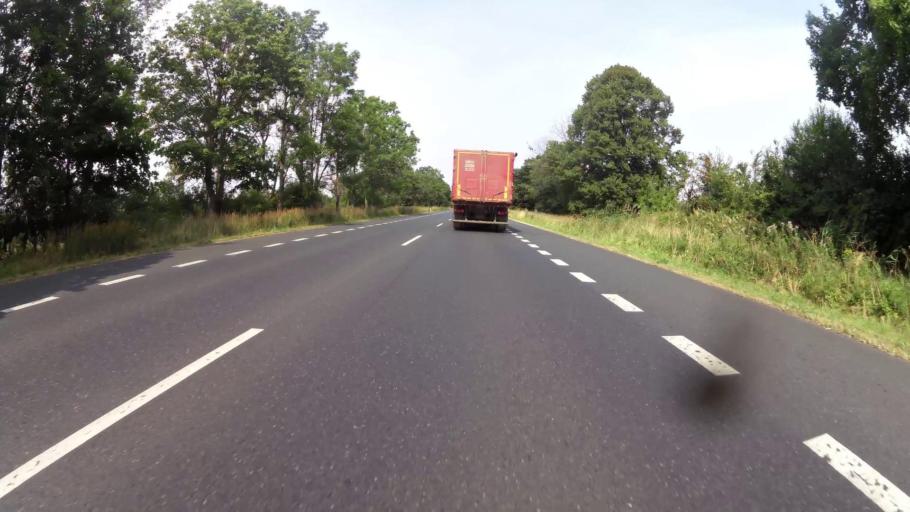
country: PL
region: West Pomeranian Voivodeship
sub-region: Powiat pyrzycki
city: Lipiany
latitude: 52.9699
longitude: 14.9711
